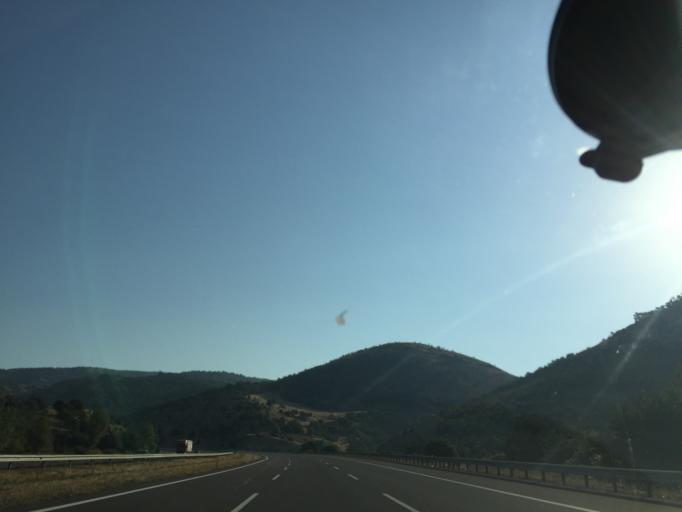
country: TR
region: Ankara
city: Celtikci
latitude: 40.3706
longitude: 32.4679
